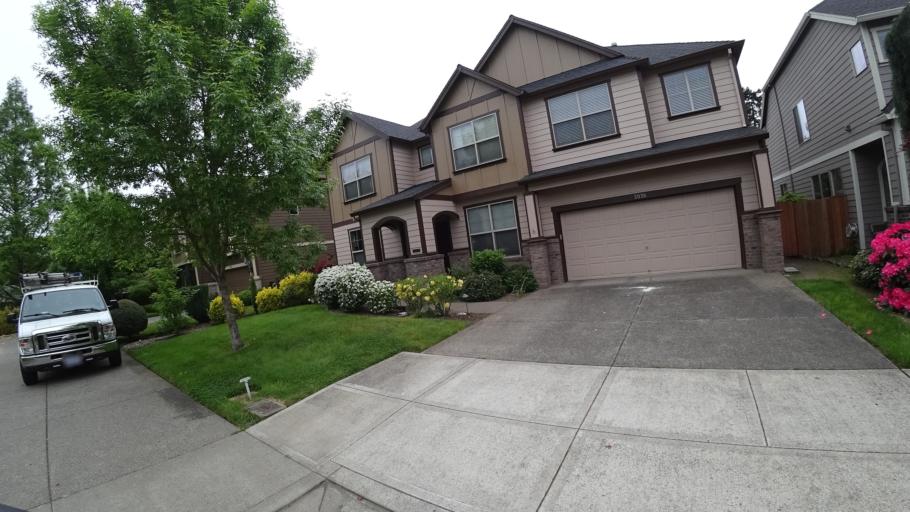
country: US
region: Oregon
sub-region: Washington County
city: Aloha
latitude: 45.5052
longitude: -122.8763
